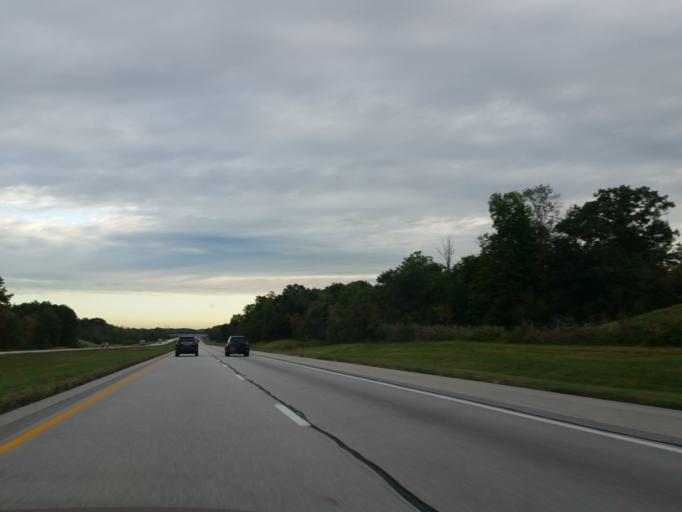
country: US
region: Ohio
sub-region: Ashtabula County
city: North Kingsville
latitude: 41.8597
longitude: -80.6905
